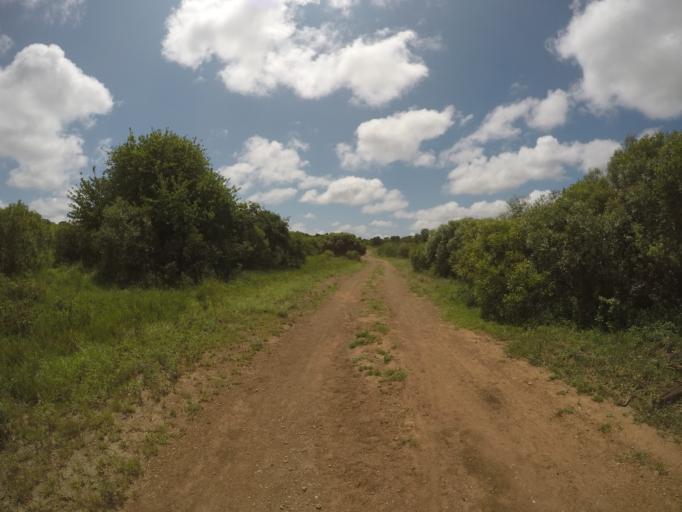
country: ZA
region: KwaZulu-Natal
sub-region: uThungulu District Municipality
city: Empangeni
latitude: -28.5801
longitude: 31.8367
